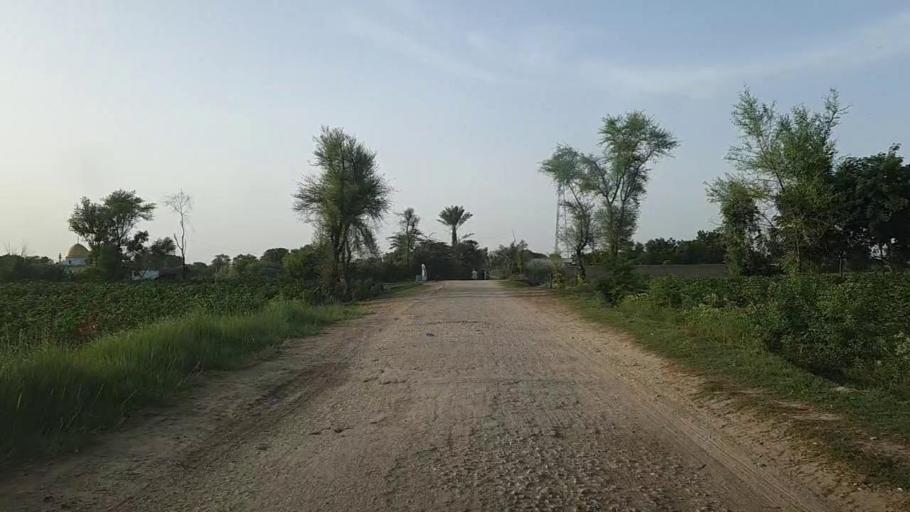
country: PK
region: Sindh
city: Bhiria
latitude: 26.9082
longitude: 68.2637
